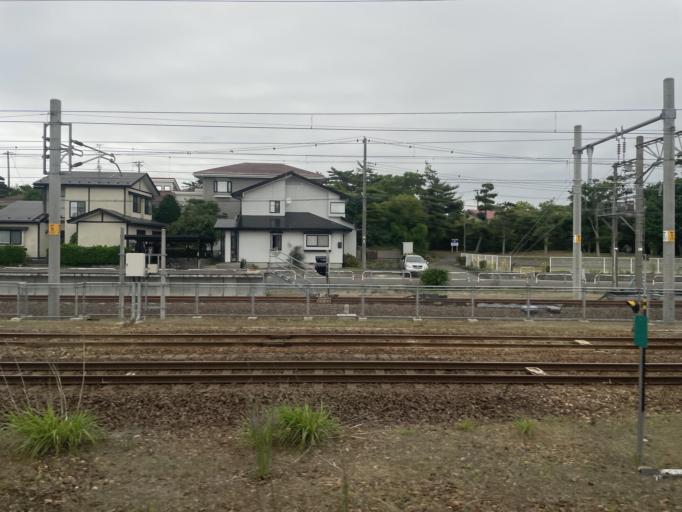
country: JP
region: Akita
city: Akita Shi
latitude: 39.8110
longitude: 140.0576
